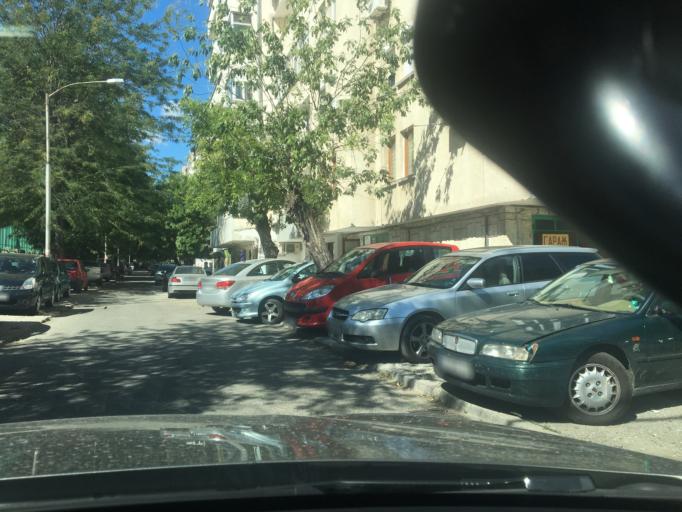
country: BG
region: Burgas
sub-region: Obshtina Burgas
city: Burgas
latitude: 42.5088
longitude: 27.4730
